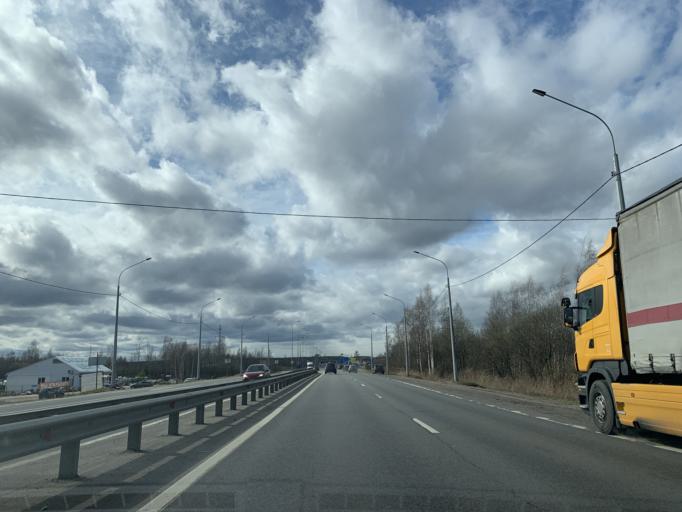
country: RU
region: Jaroslavl
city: Yaroslavl
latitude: 57.6825
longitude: 39.9161
